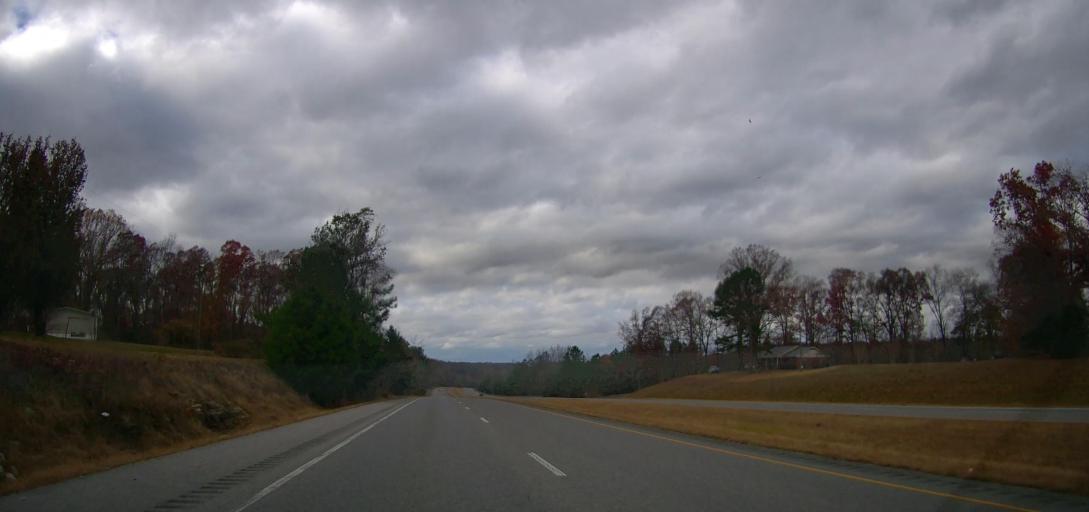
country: US
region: Alabama
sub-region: Lawrence County
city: Town Creek
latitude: 34.5990
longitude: -87.4412
